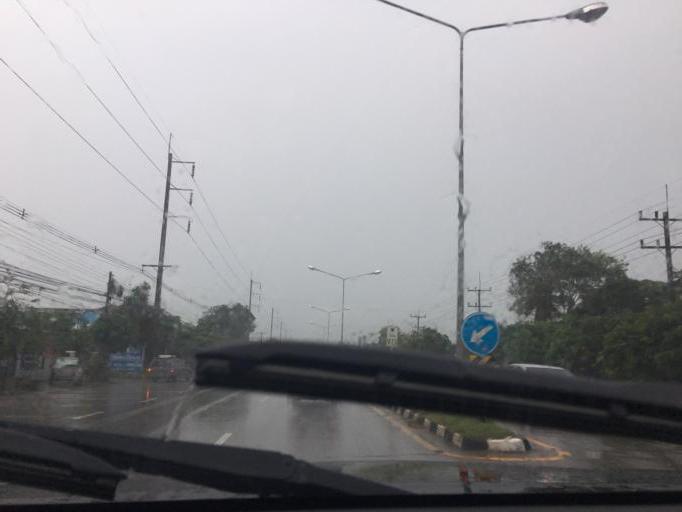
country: TH
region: Chiang Rai
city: Mae Fa Luang
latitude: 20.2383
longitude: 99.8561
